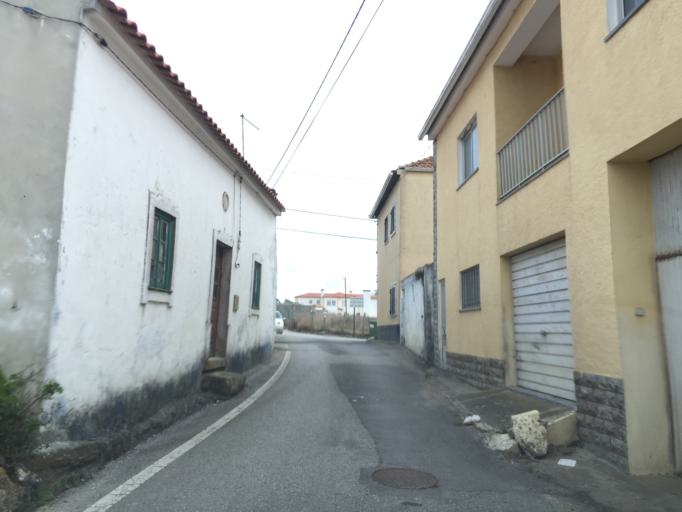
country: PT
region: Leiria
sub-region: Peniche
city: Atouguia da Baleia
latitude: 39.3419
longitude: -9.2948
